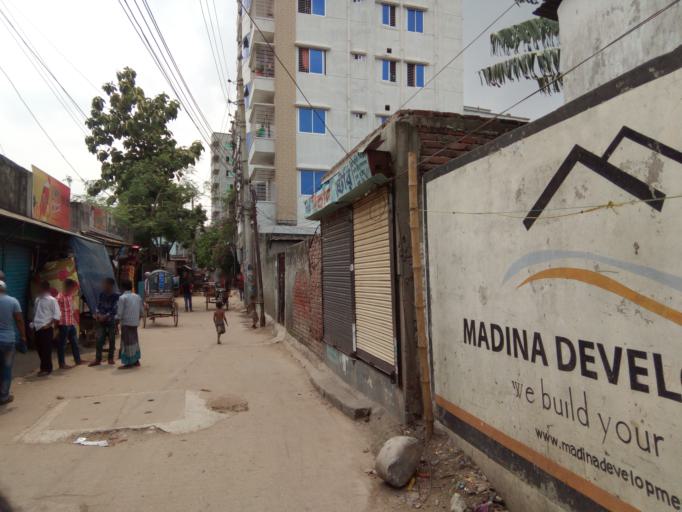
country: BD
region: Dhaka
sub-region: Dhaka
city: Dhaka
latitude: 23.6984
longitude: 90.4334
